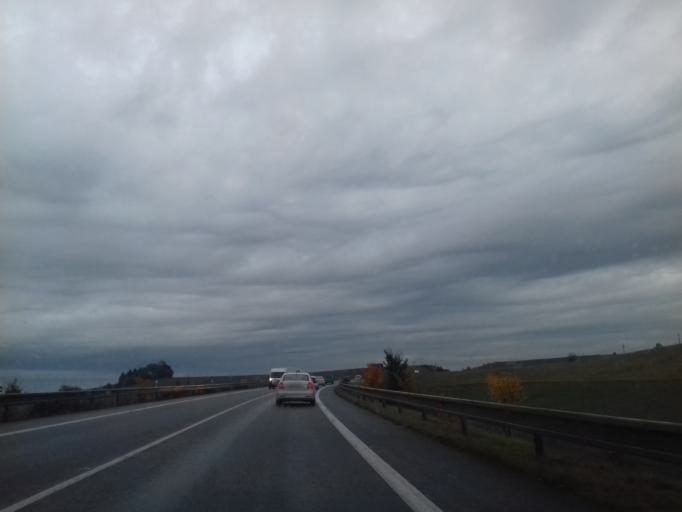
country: CZ
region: Pardubicky
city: Holice
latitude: 50.0634
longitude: 15.9764
